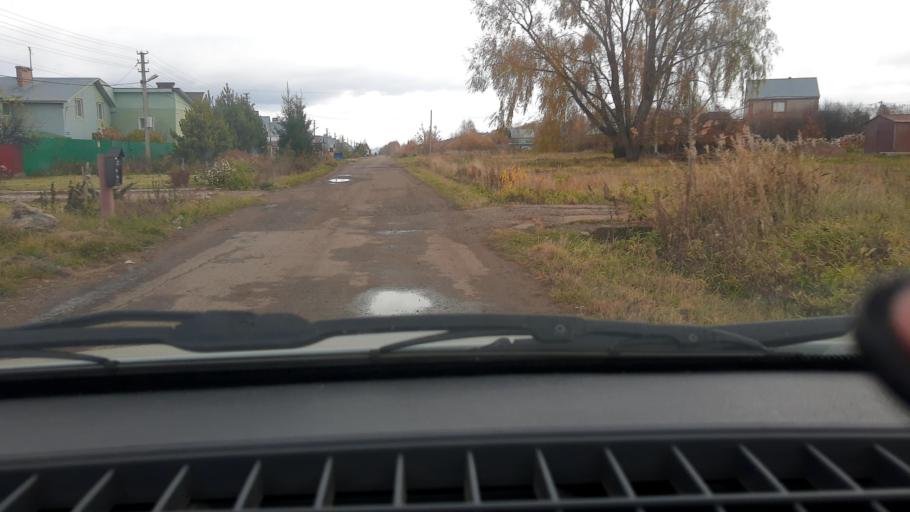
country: RU
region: Bashkortostan
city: Avdon
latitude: 54.6904
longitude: 55.7860
